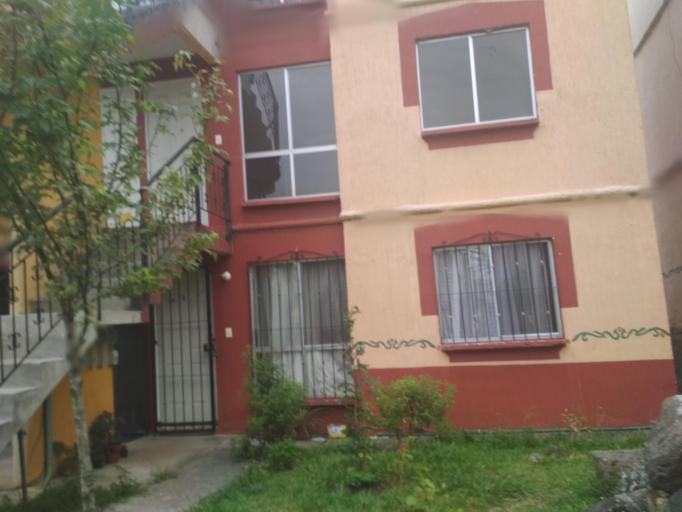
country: MX
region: Veracruz
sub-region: Coatepec
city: Las Lomas
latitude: 19.4180
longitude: -96.9286
